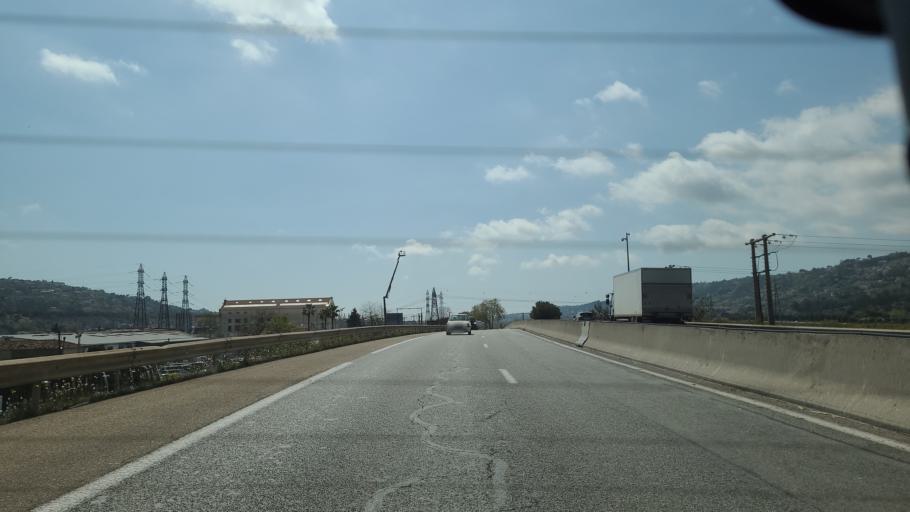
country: FR
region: Provence-Alpes-Cote d'Azur
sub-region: Departement des Alpes-Maritimes
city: La Gaude
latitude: 43.7229
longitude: 7.1861
